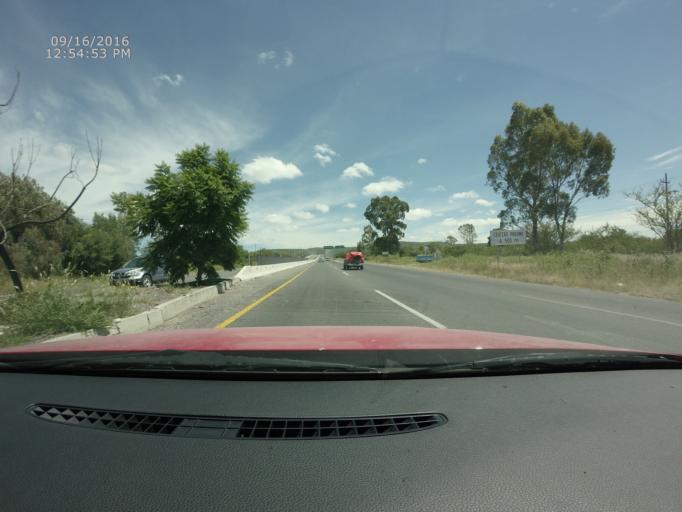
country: MX
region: Queretaro
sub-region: Colon
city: Purisima de Cubos (La Purisima)
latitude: 20.6360
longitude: -100.1132
